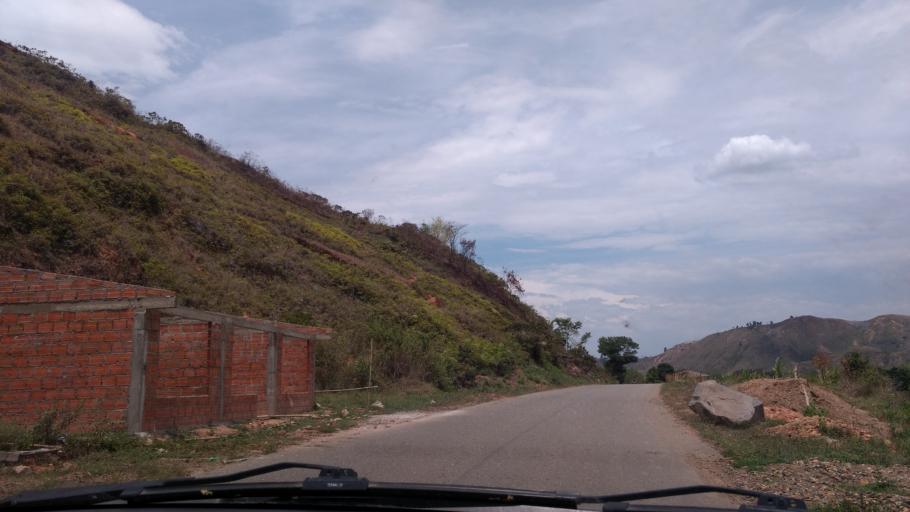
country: CO
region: Cauca
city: Buenos Aires
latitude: 3.0428
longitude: -76.6686
